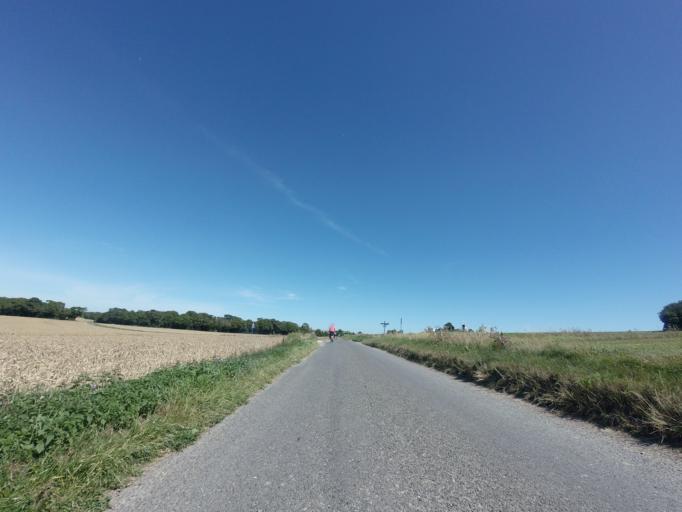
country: GB
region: England
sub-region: Kent
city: Deal
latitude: 51.1920
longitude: 1.3719
